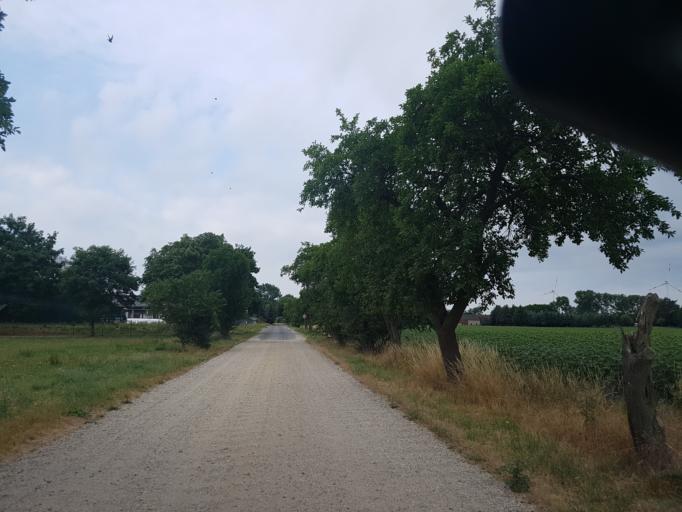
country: DE
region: Brandenburg
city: Doberlug-Kirchhain
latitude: 51.6943
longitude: 13.5192
